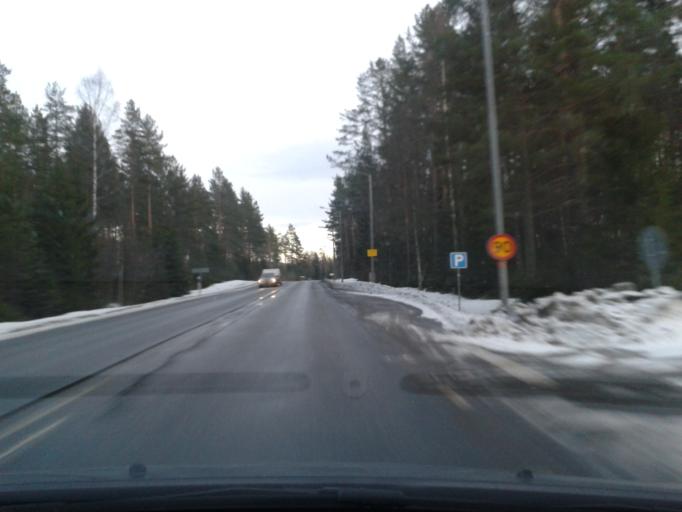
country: SE
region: Vaesternorrland
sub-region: Solleftea Kommun
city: Solleftea
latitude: 63.1550
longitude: 17.3275
